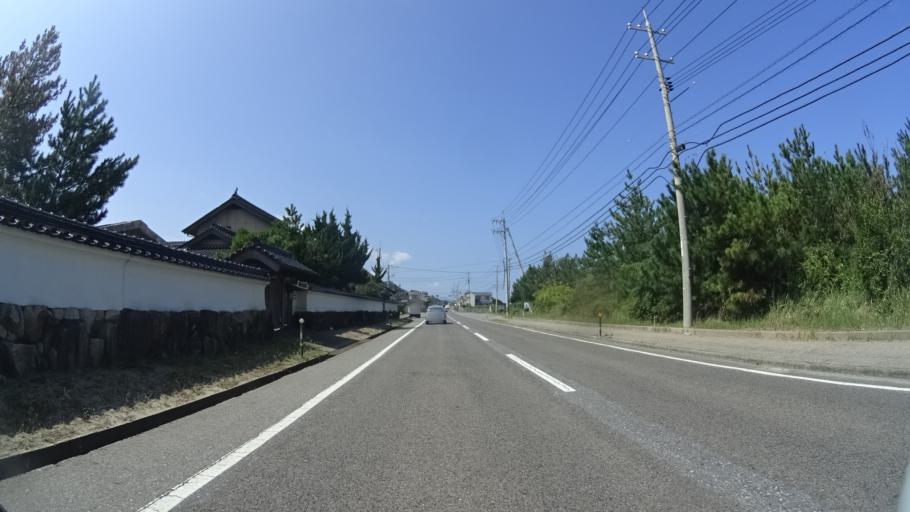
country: JP
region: Shimane
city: Masuda
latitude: 34.6872
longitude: 131.7964
